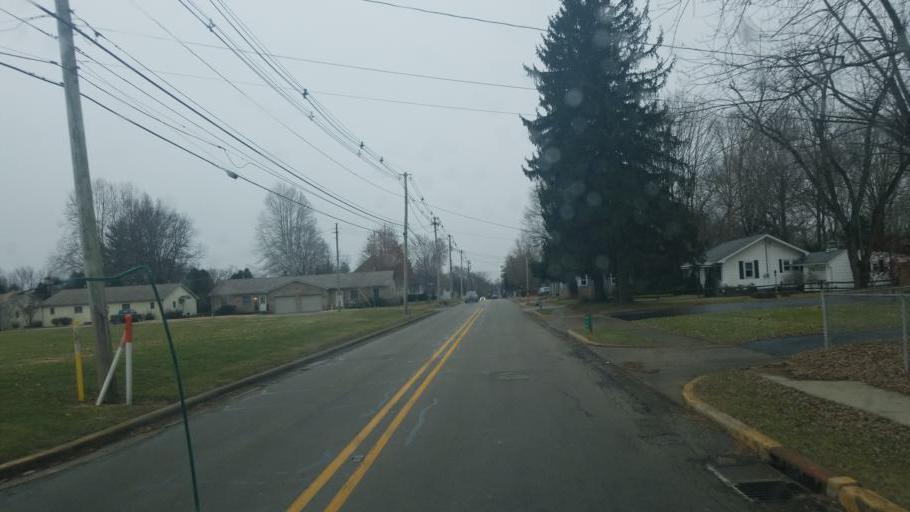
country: US
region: Indiana
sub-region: Henry County
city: Knightstown
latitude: 39.7999
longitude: -85.5322
